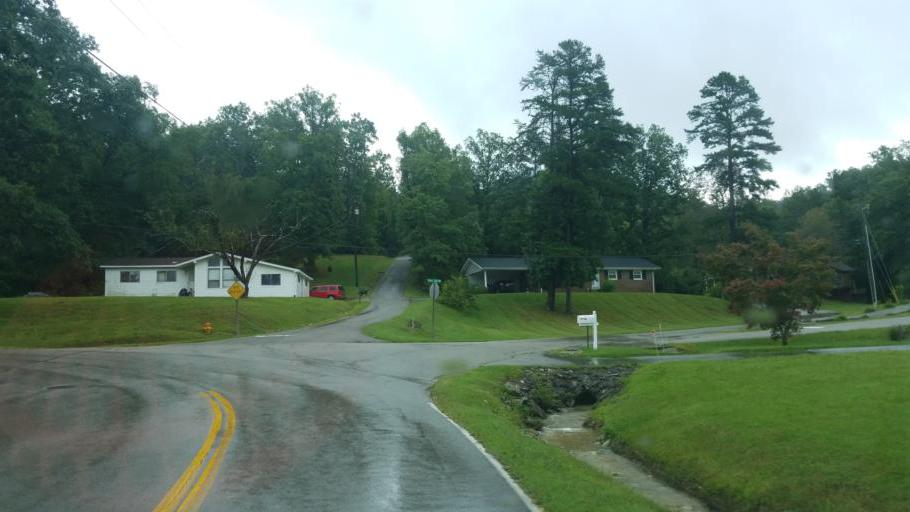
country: US
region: Kentucky
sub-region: Rowan County
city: Morehead
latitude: 38.1812
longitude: -83.4831
